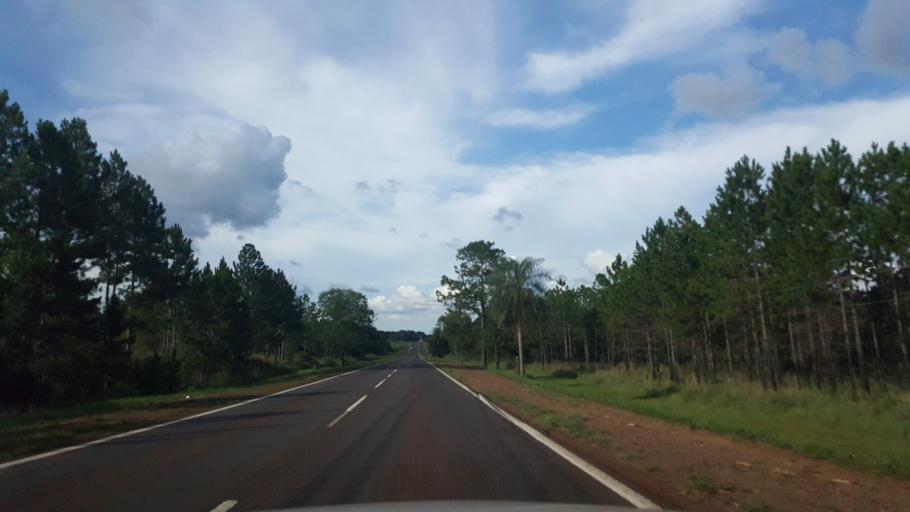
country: AR
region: Misiones
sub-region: Departamento de Candelaria
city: Loreto
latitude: -27.3448
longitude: -55.5465
